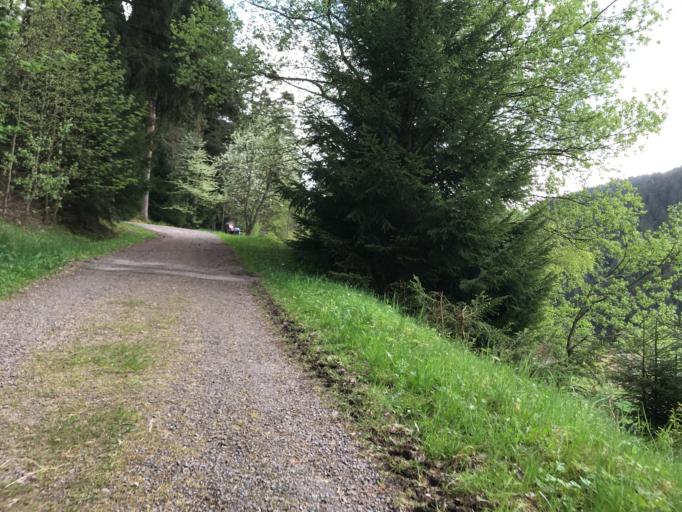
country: DE
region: Baden-Wuerttemberg
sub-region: Karlsruhe Region
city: Baiersbronn
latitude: 48.4958
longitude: 8.3638
